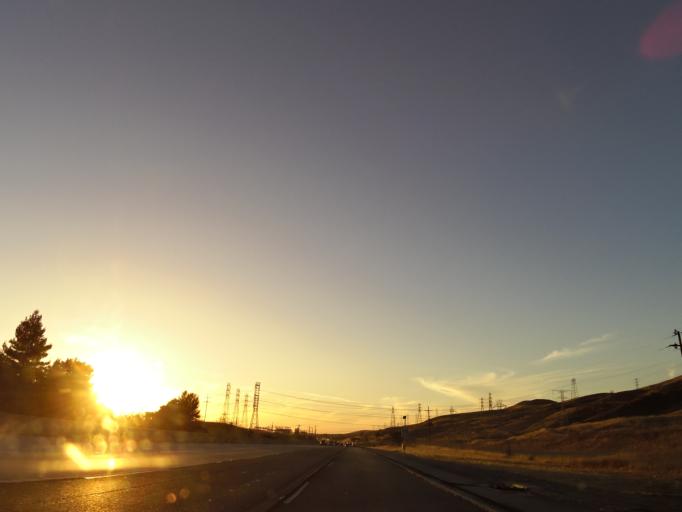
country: US
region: California
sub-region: Santa Clara County
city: Seven Trees
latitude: 37.2216
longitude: -121.7358
